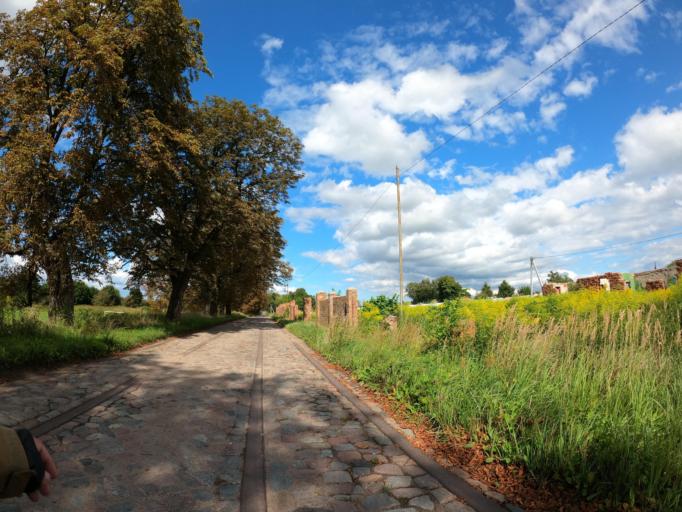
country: RU
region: Kaliningrad
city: Zheleznodorozhnyy
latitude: 54.3545
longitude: 21.3214
